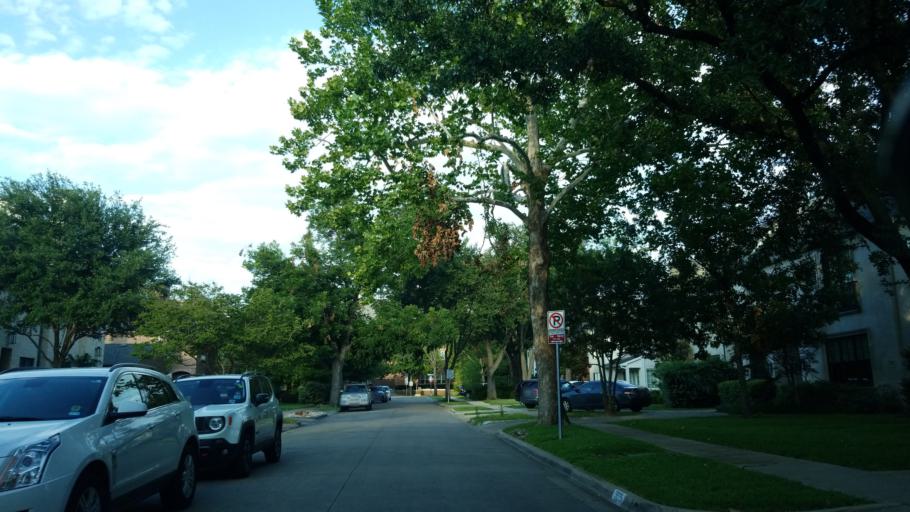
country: US
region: Texas
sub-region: Dallas County
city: Highland Park
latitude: 32.8412
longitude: -96.7933
